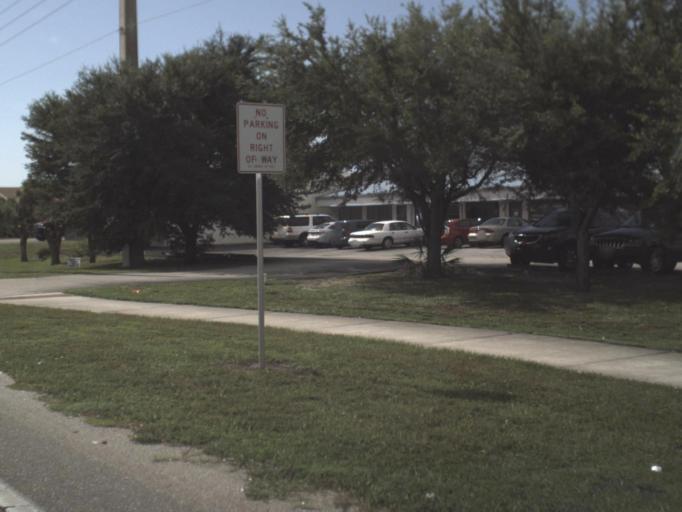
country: US
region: Florida
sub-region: Charlotte County
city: Port Charlotte
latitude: 26.9944
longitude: -82.1162
